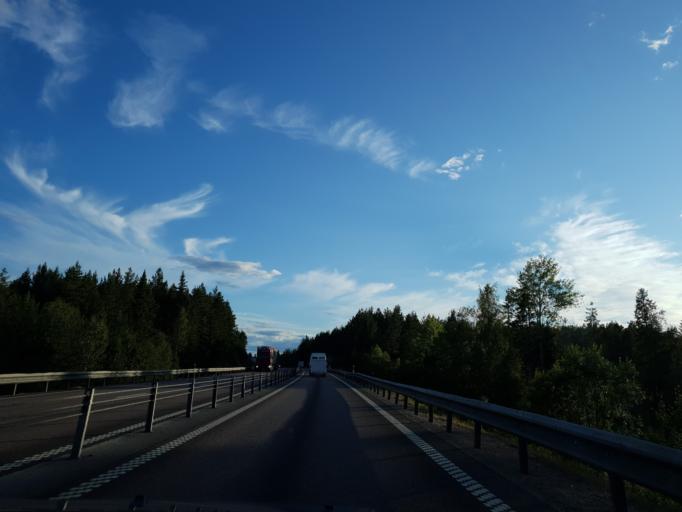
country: SE
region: Gaevleborg
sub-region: Hudiksvalls Kommun
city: Hudiksvall
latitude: 61.7733
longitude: 17.1062
